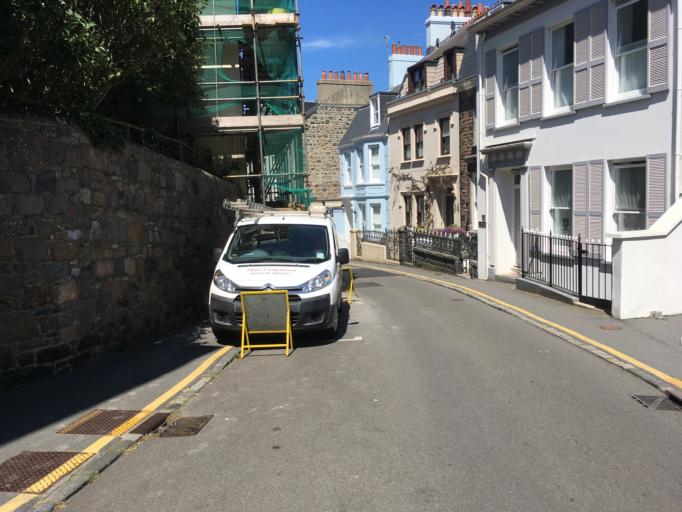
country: GG
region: St Peter Port
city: Saint Peter Port
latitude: 49.4517
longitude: -2.5374
